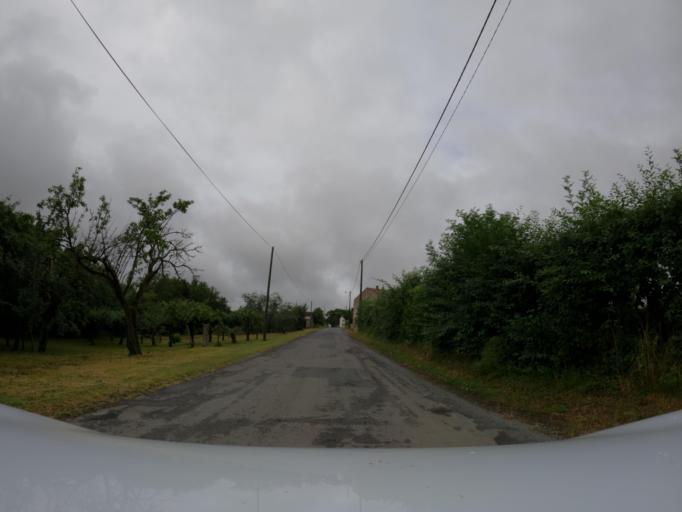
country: FR
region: Pays de la Loire
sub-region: Departement de la Vendee
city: Maillezais
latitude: 46.4057
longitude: -0.7118
